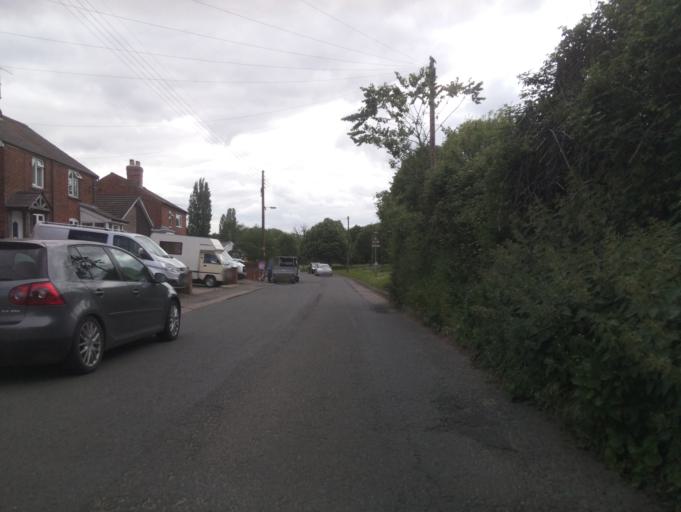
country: GB
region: England
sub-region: Herefordshire
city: Ledbury
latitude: 52.0344
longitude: -2.4373
